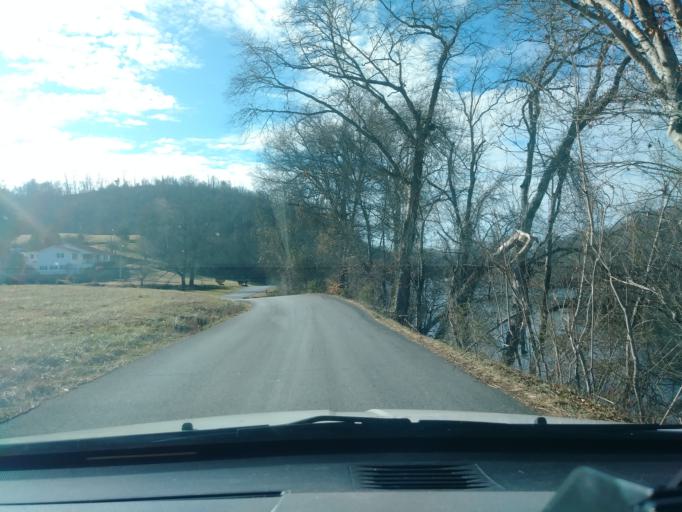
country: US
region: Tennessee
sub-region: Cocke County
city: Newport
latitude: 35.9781
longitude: -83.1482
